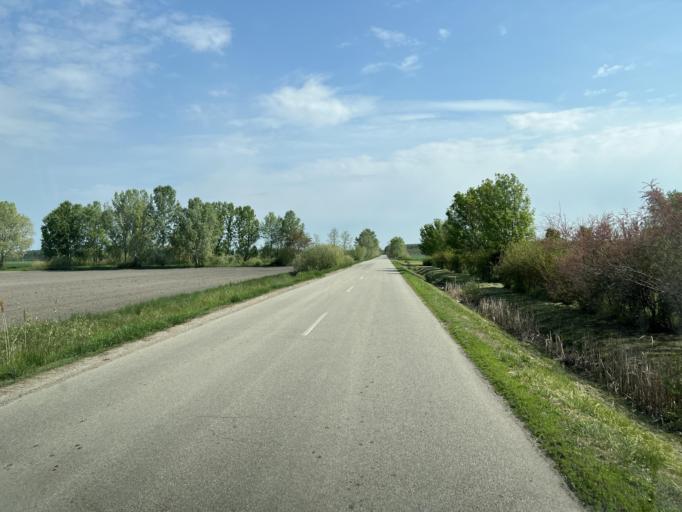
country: HU
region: Pest
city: Kocser
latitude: 47.0056
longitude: 19.9248
